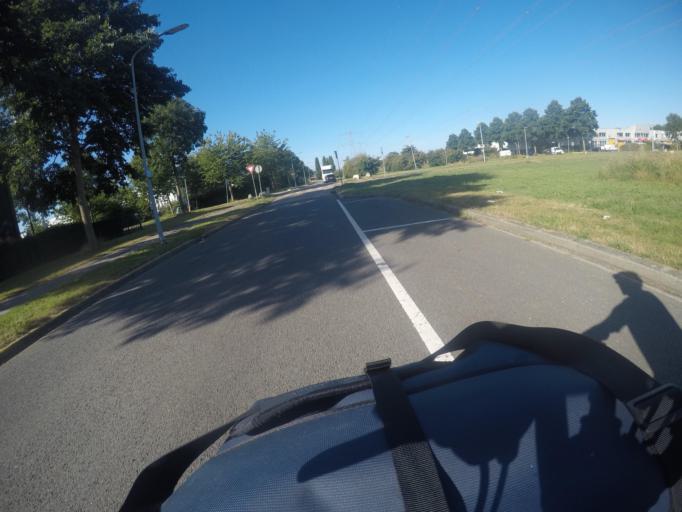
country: NL
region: Flevoland
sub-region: Gemeente Almere
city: Almere Stad
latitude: 52.3502
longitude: 5.1877
